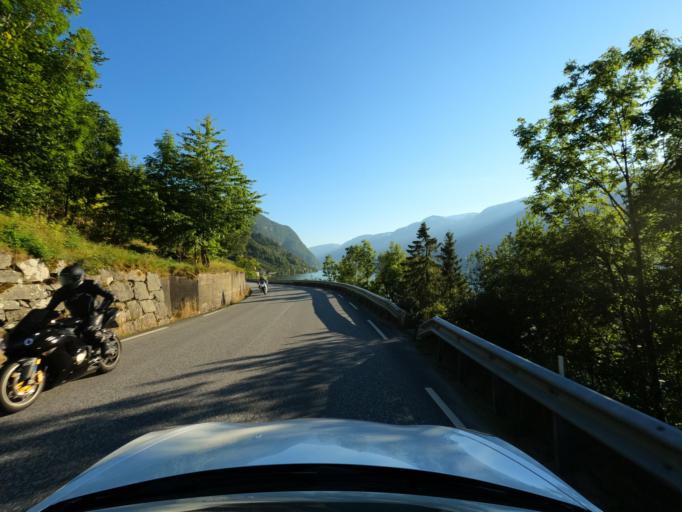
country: NO
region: Hordaland
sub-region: Odda
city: Odda
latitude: 60.2117
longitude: 6.6023
